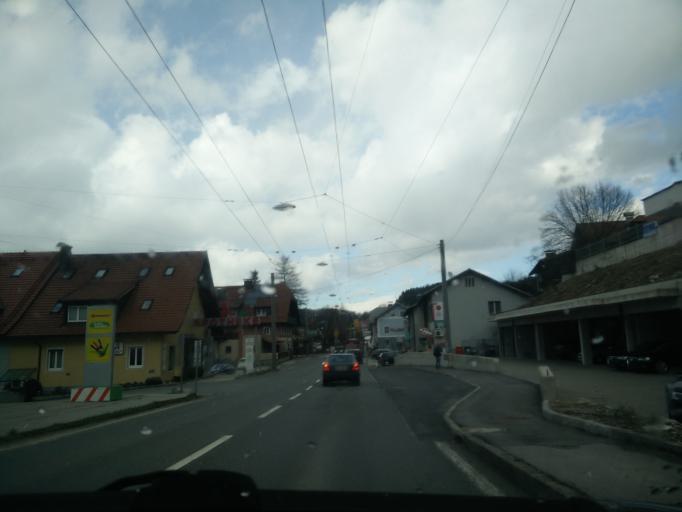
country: AT
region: Salzburg
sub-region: Politischer Bezirk Salzburg-Umgebung
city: Hallwang
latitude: 47.8304
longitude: 13.0842
